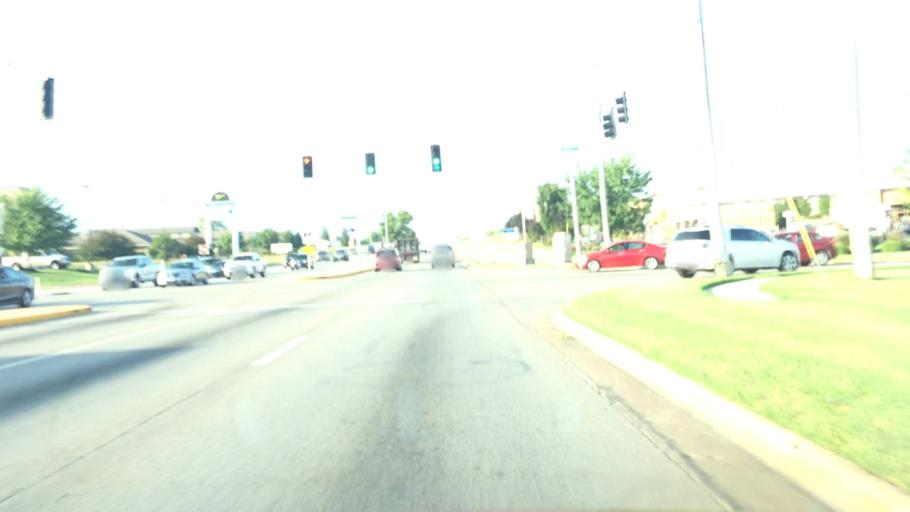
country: US
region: Missouri
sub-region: Greene County
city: Springfield
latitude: 37.1673
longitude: -93.3163
